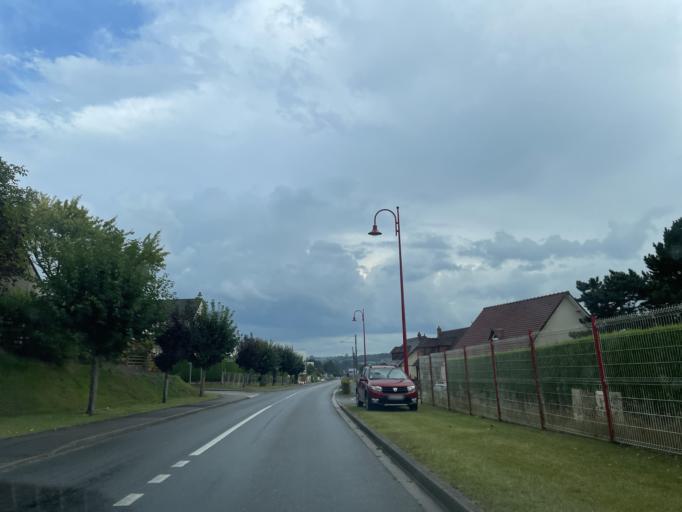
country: FR
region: Haute-Normandie
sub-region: Departement de la Seine-Maritime
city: Neufchatel-en-Bray
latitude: 49.7414
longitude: 1.4375
